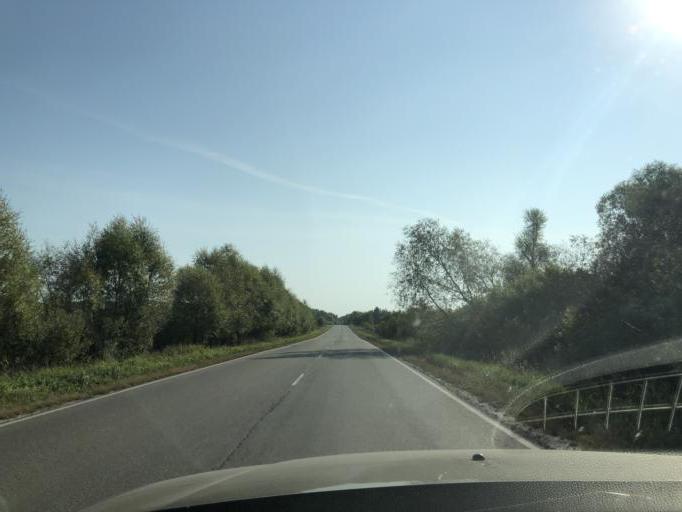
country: RU
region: Tula
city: Novogurovskiy
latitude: 54.4484
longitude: 37.3906
